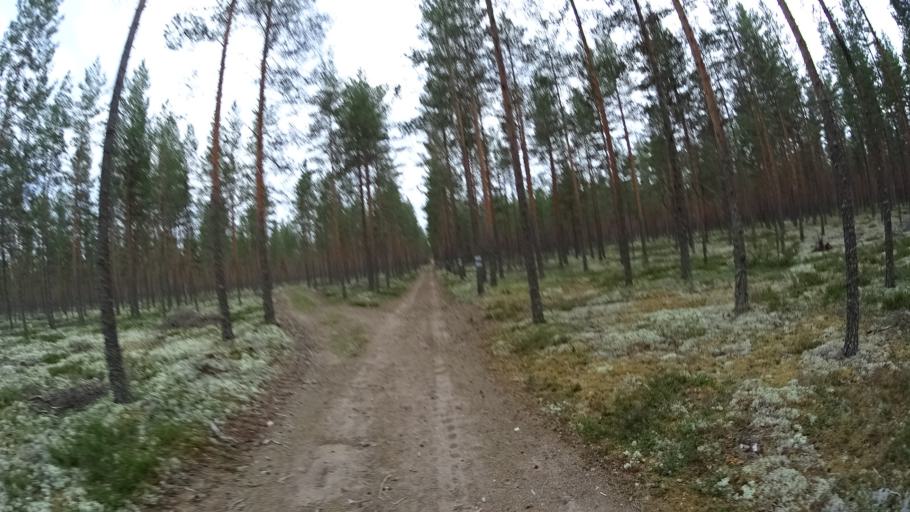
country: FI
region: Satakunta
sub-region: Pohjois-Satakunta
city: Jaemijaervi
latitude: 61.7662
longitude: 22.8011
